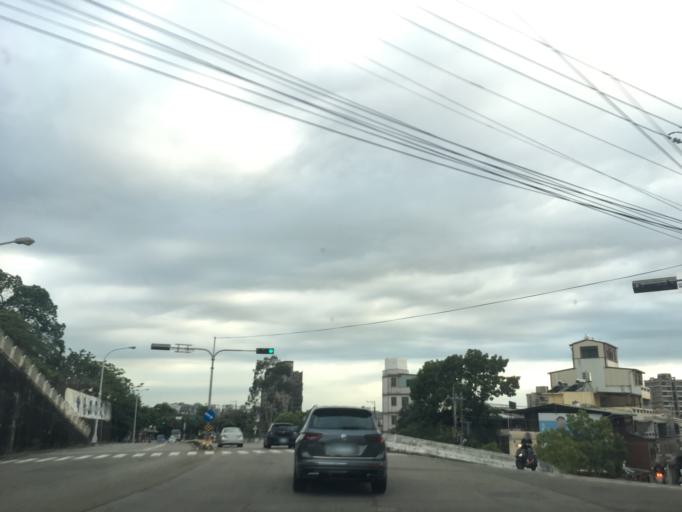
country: TW
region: Taiwan
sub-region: Taichung City
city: Taichung
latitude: 24.1738
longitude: 120.7345
